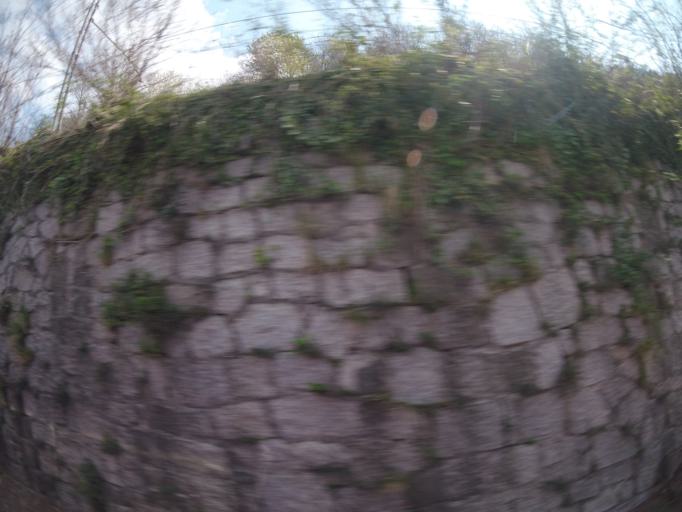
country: IT
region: Piedmont
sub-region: Provincia Verbano-Cusio-Ossola
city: Nonio
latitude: 45.8486
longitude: 8.4062
